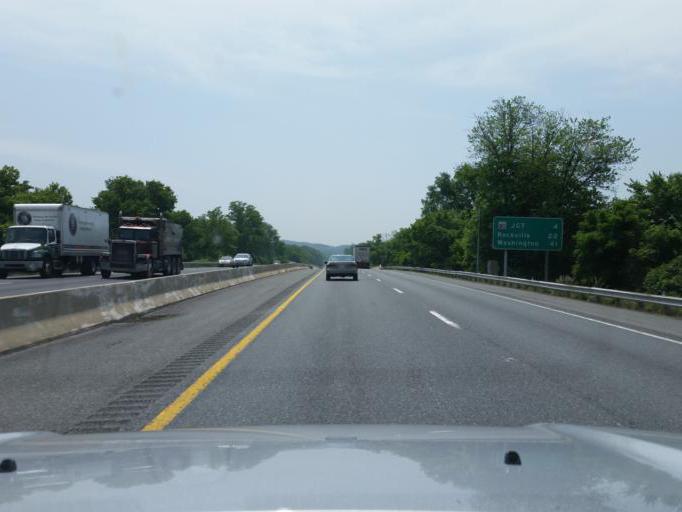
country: US
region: Maryland
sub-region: Frederick County
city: Ballenger Creek
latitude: 39.3705
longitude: -77.4033
